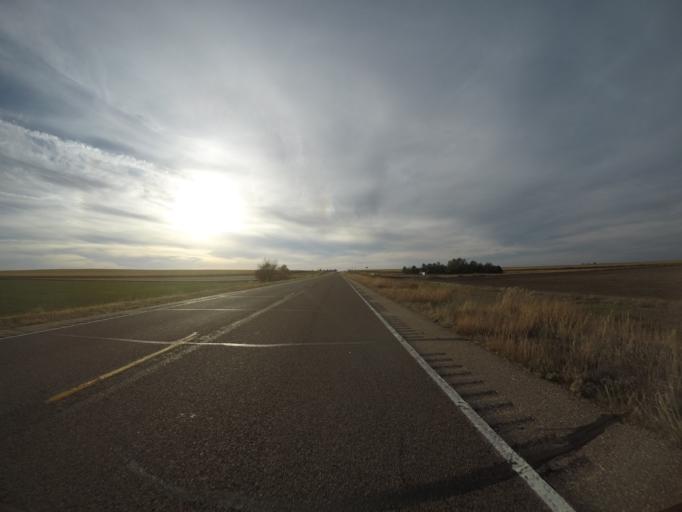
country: US
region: Colorado
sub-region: Kit Carson County
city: Burlington
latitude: 39.6580
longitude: -102.5162
